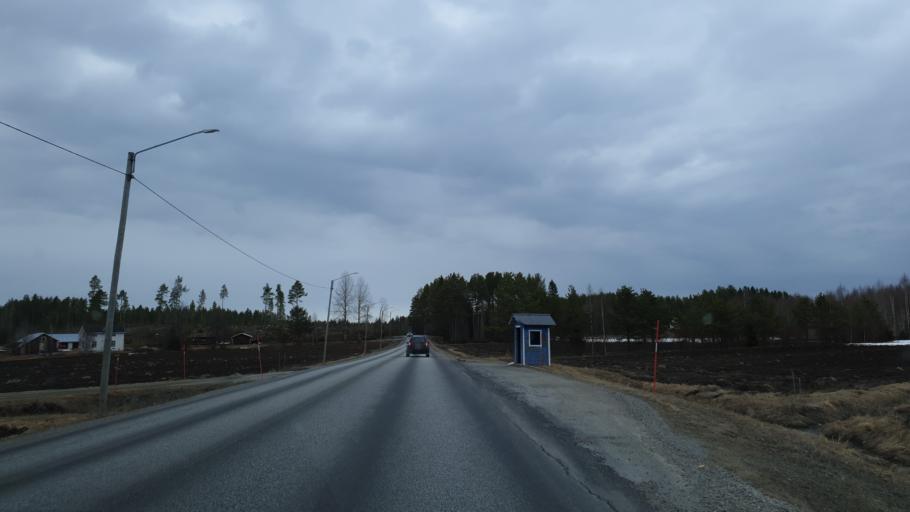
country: SE
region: Vaesterbotten
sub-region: Skelleftea Kommun
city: Viken
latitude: 64.6456
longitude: 20.9590
